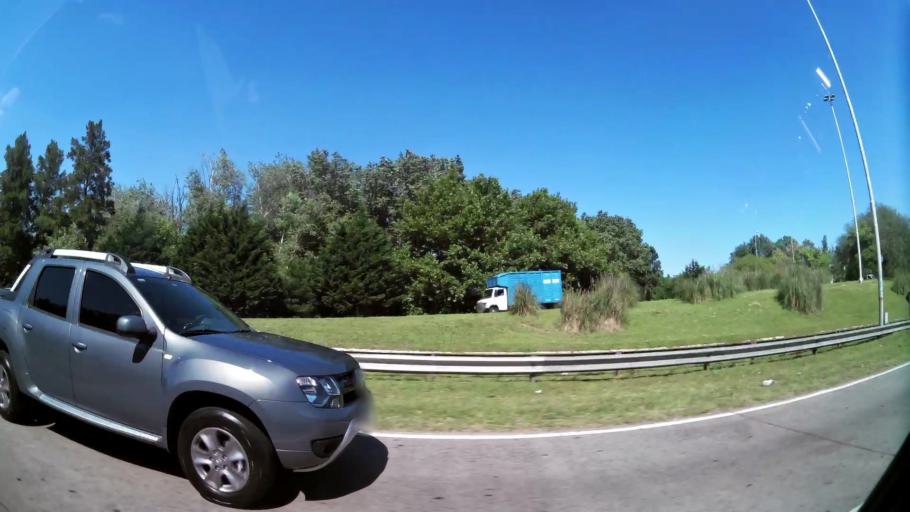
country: AR
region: Buenos Aires
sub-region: Partido de San Isidro
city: San Isidro
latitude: -34.4789
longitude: -58.5627
